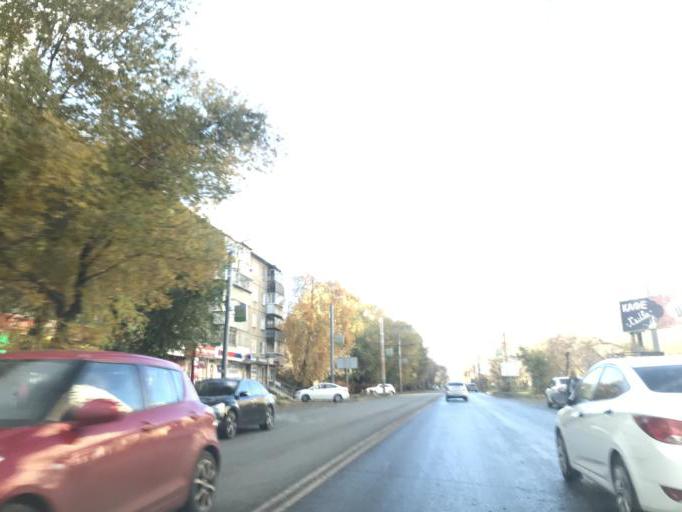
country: RU
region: Chelyabinsk
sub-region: Gorod Chelyabinsk
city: Chelyabinsk
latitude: 55.1720
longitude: 61.4519
